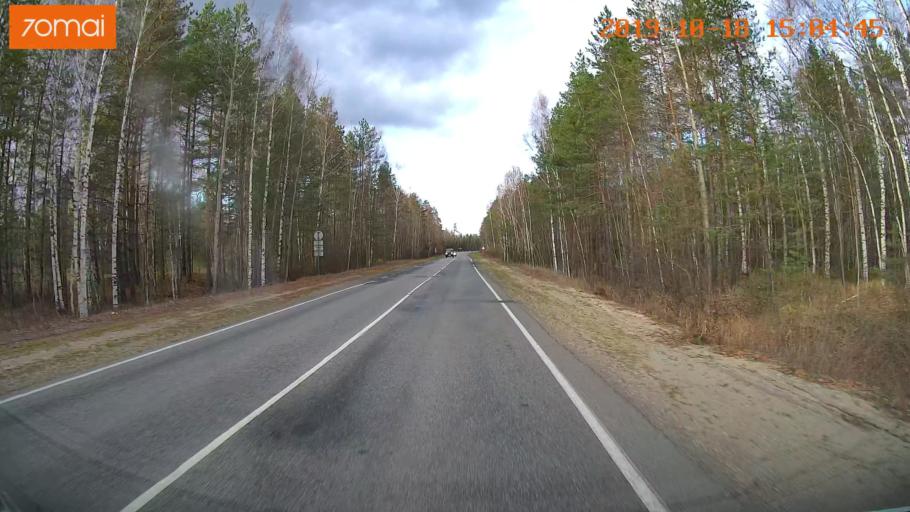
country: RU
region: Vladimir
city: Kurlovo
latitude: 55.5058
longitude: 40.5711
